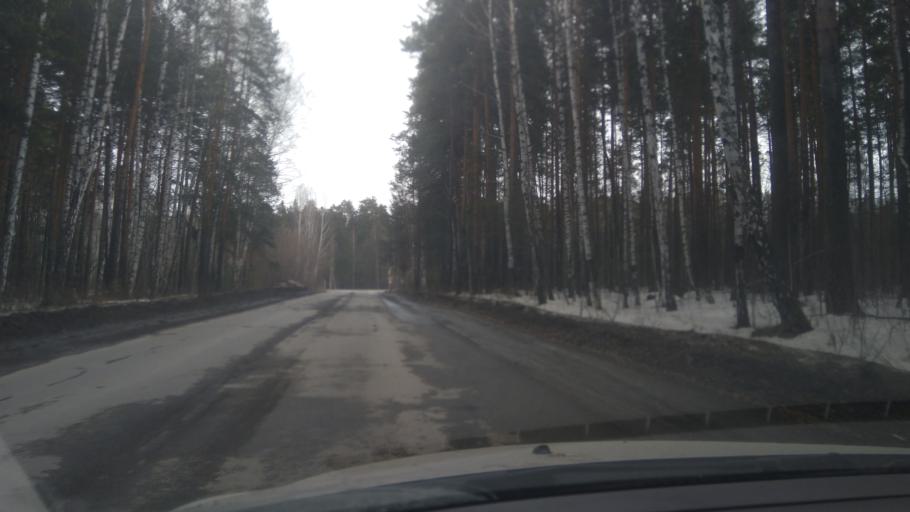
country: RU
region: Sverdlovsk
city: Severka
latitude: 56.8343
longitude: 60.3837
